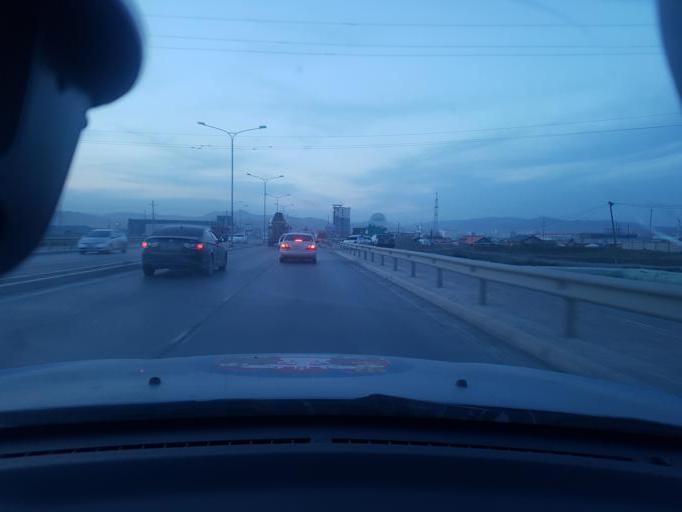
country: MN
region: Ulaanbaatar
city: Ulaanbaatar
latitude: 47.8859
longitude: 106.7854
